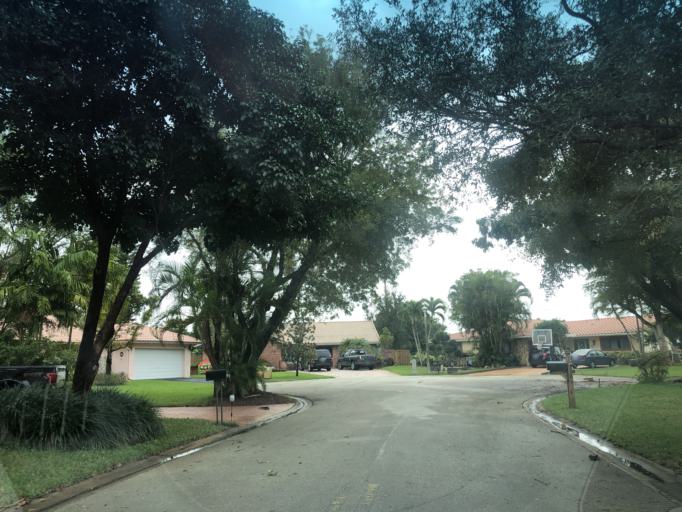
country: US
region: Florida
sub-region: Broward County
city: North Lauderdale
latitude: 26.2313
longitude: -80.2378
